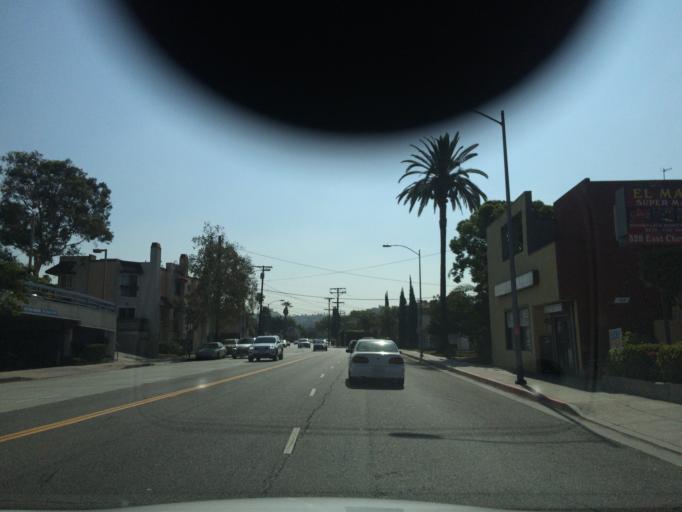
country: US
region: California
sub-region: Los Angeles County
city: Glendale
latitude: 34.1335
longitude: -118.2515
